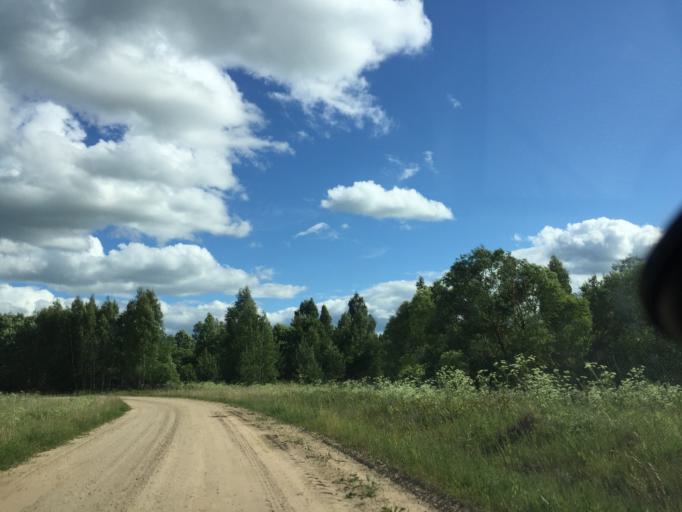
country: LV
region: Vecumnieki
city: Vecumnieki
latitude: 56.4191
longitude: 24.6143
